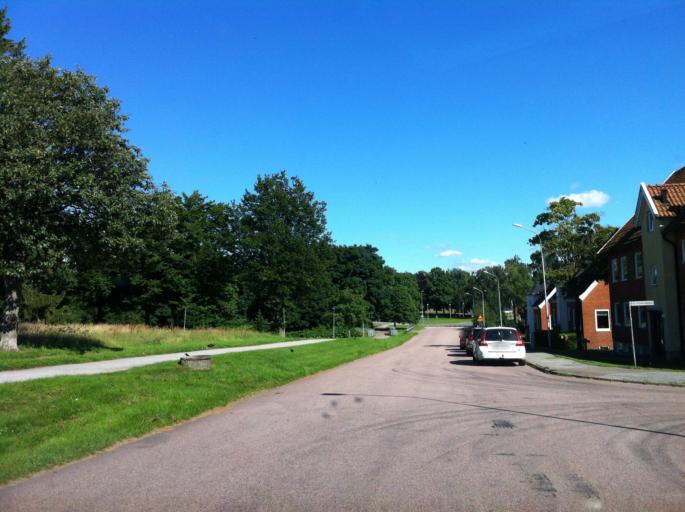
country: SE
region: Skane
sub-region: Svalovs Kommun
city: Kagerod
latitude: 56.0231
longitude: 13.1113
